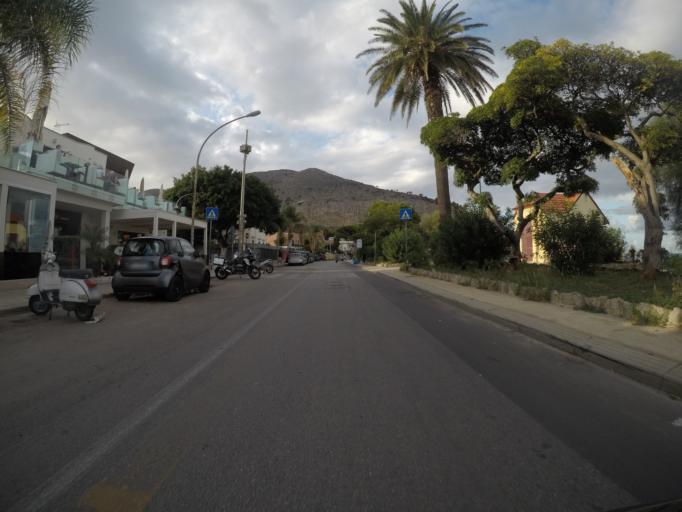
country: IT
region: Sicily
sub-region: Palermo
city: Palermo
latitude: 38.2033
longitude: 13.3257
